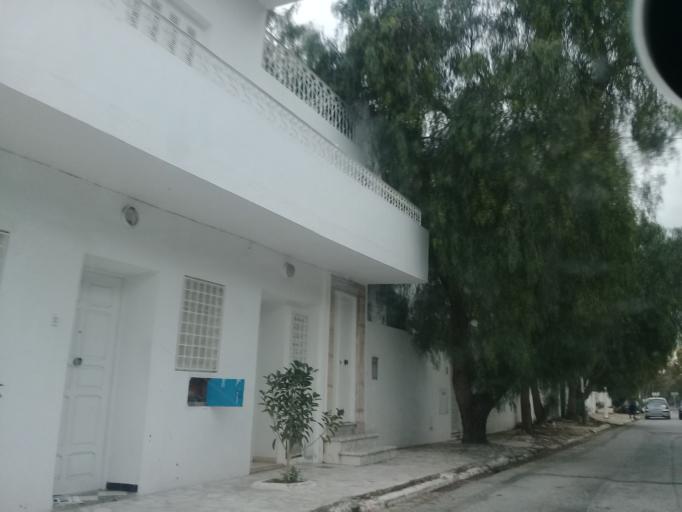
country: TN
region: Tunis
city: Sidi Bou Said
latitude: 36.8669
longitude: 10.3373
